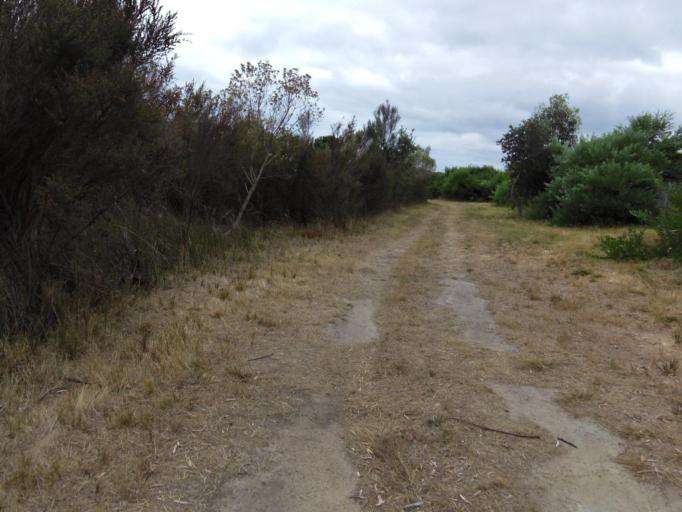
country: AU
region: Victoria
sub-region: Mornington Peninsula
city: Mount Martha
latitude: -38.2840
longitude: 145.0111
